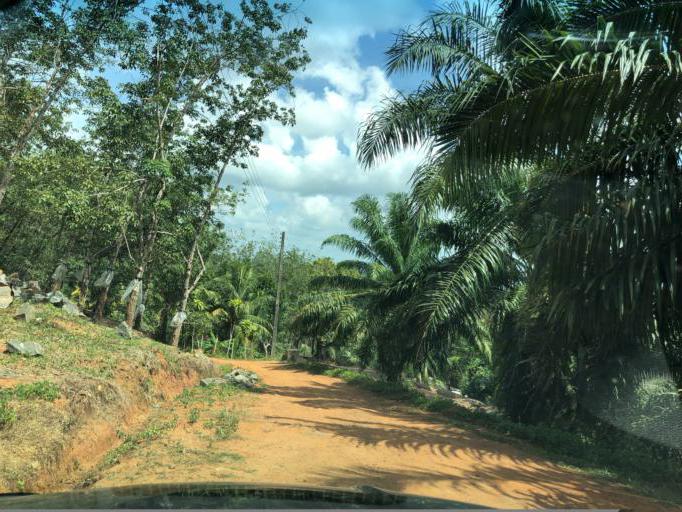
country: LK
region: Western
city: Horawala Junction
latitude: 6.5491
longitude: 80.0894
